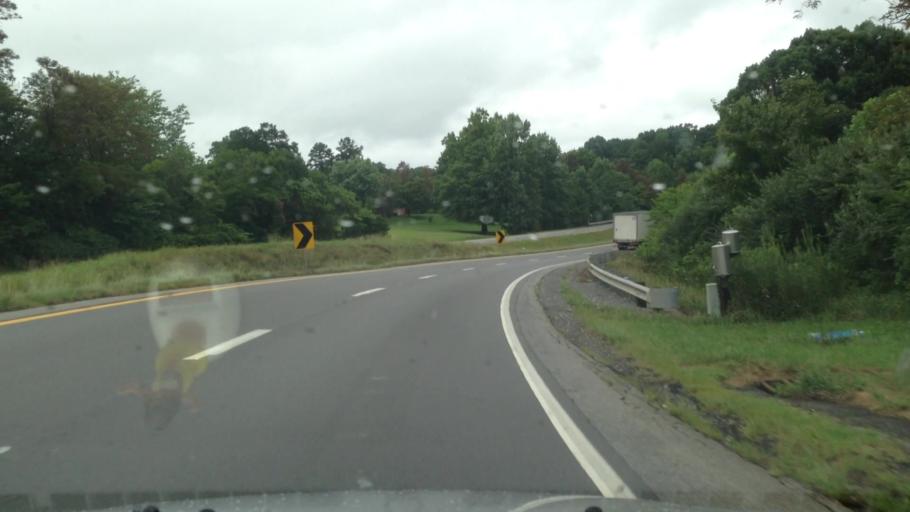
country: US
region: Virginia
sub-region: Henry County
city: Stanleytown
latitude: 36.8083
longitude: -79.9388
